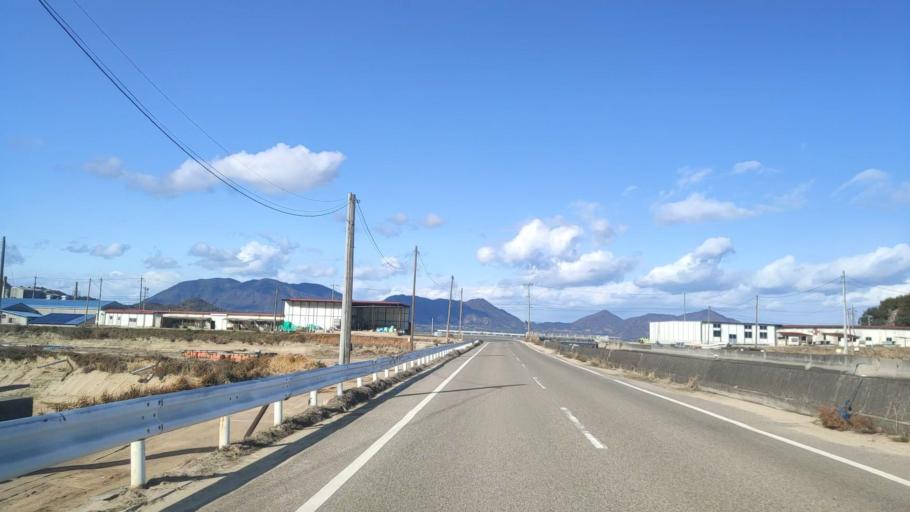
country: JP
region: Hiroshima
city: Innoshima
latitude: 34.2146
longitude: 133.1217
